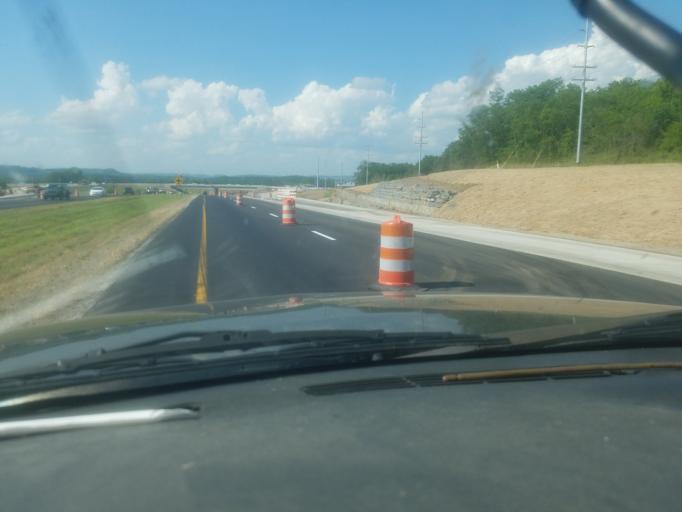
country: US
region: Tennessee
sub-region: Maury County
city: Mount Pleasant
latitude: 35.5394
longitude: -87.2212
